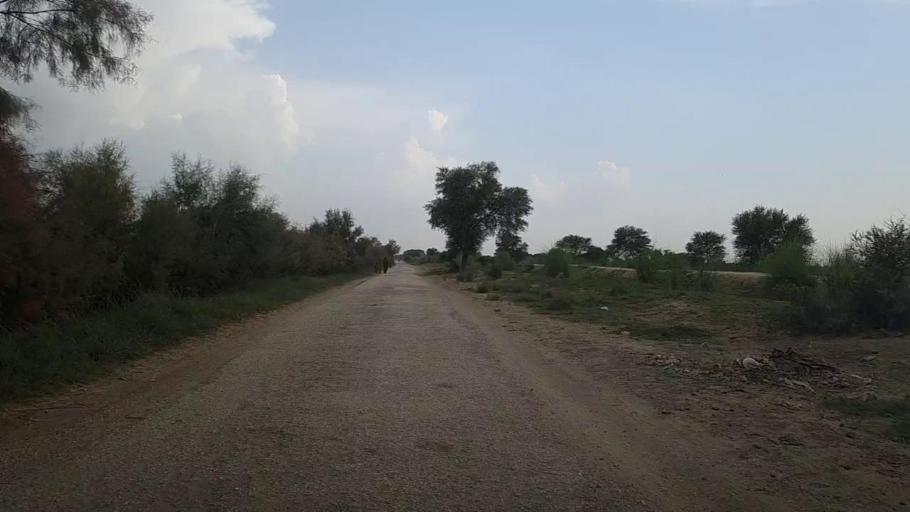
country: PK
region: Sindh
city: Khanpur
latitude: 27.8502
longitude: 69.4857
